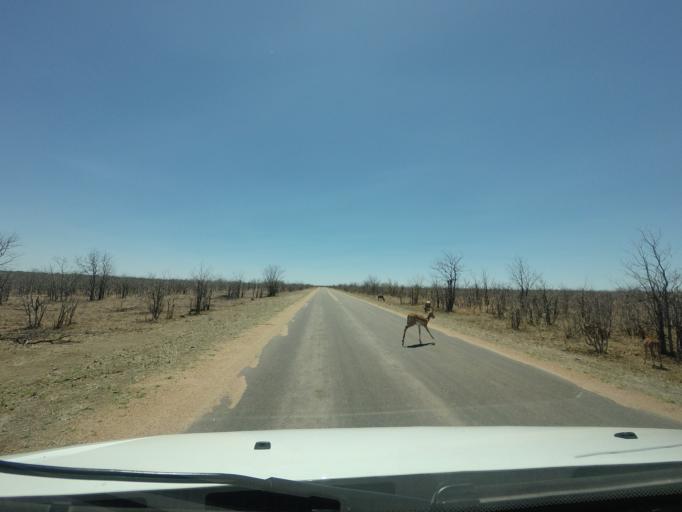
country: ZA
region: Limpopo
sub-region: Mopani District Municipality
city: Phalaborwa
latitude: -23.5725
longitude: 31.4516
